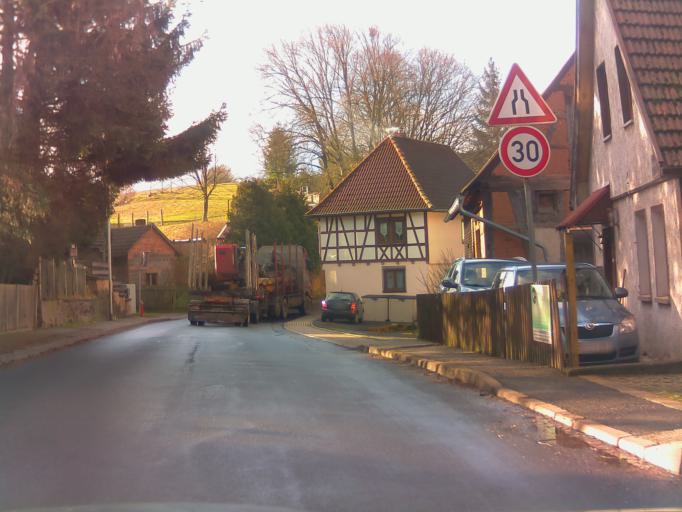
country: DE
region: Thuringia
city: Rosa
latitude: 50.7166
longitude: 10.2634
